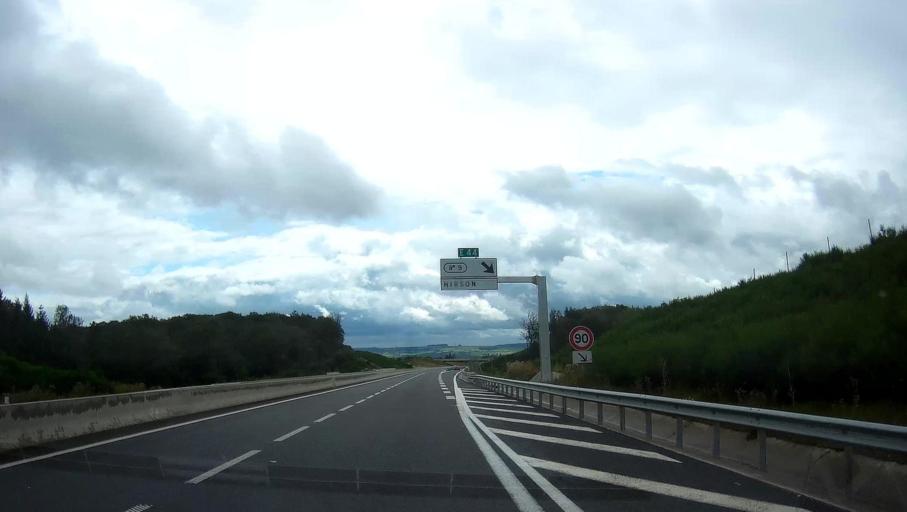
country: FR
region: Champagne-Ardenne
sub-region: Departement des Ardennes
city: Rimogne
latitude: 49.8506
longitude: 4.5133
